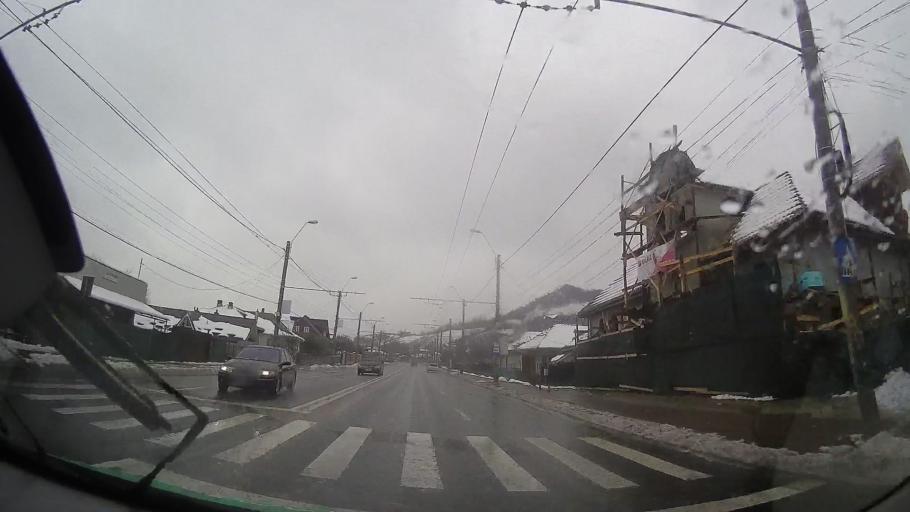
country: RO
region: Neamt
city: Piatra Neamt
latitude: 46.9402
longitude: 26.3311
